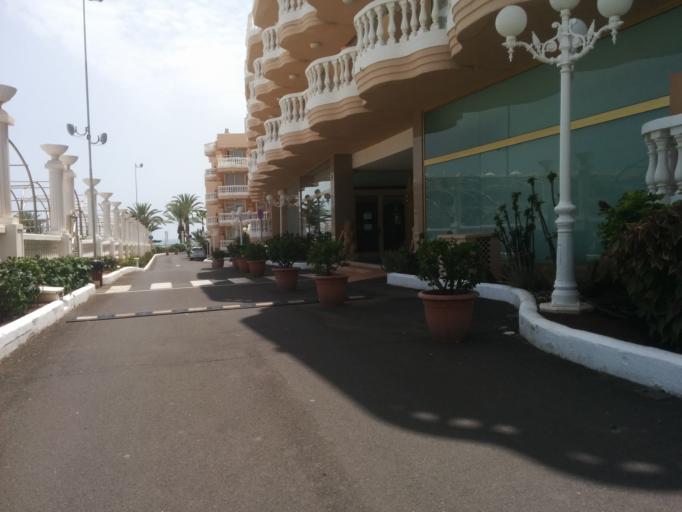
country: ES
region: Canary Islands
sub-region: Provincia de Santa Cruz de Tenerife
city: Playa de las Americas
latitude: 28.0542
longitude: -16.7307
